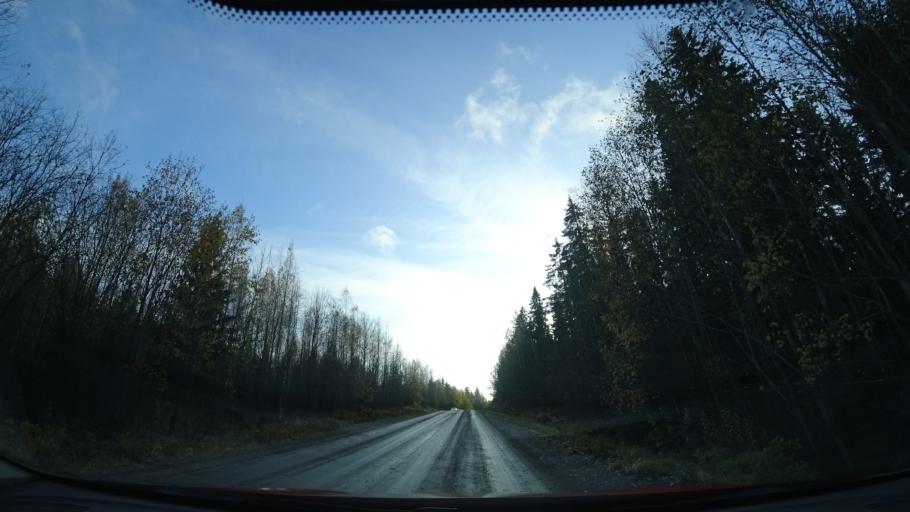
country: FI
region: Uusimaa
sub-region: Helsinki
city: Sibbo
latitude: 60.2935
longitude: 25.1990
